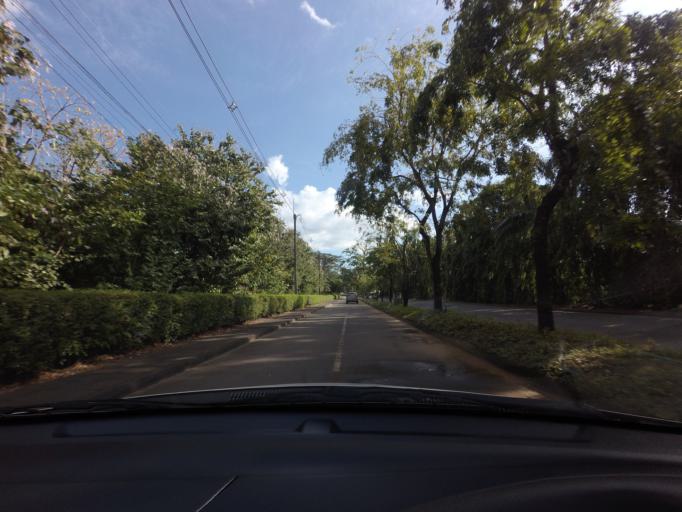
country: TH
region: Nakhon Nayok
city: Nakhon Nayok
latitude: 14.3224
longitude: 101.3048
